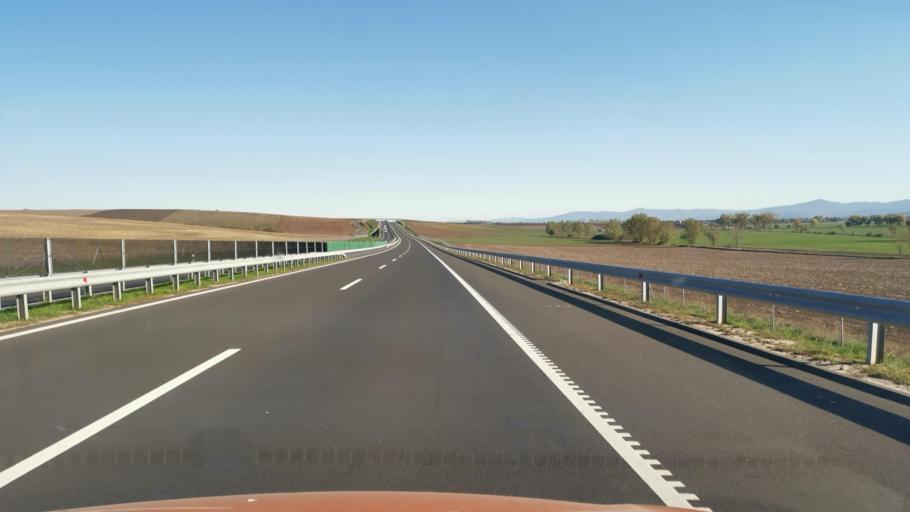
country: HU
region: Borsod-Abauj-Zemplen
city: Halmaj
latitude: 48.2672
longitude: 20.9955
